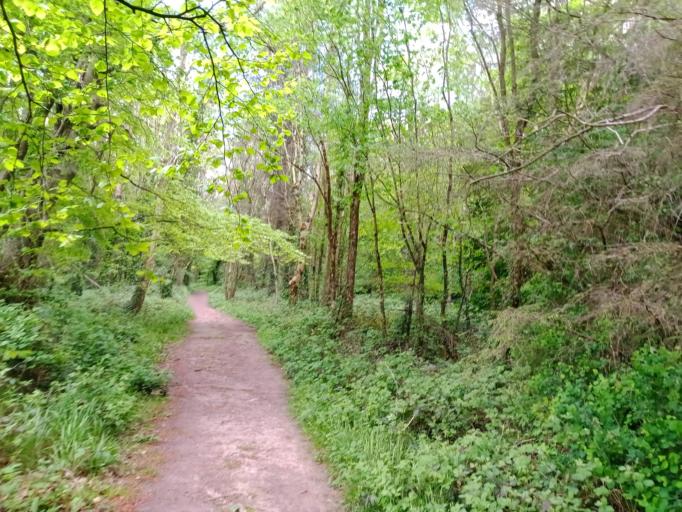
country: IE
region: Leinster
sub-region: Kilkenny
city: Castlecomer
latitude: 52.8188
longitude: -7.2054
